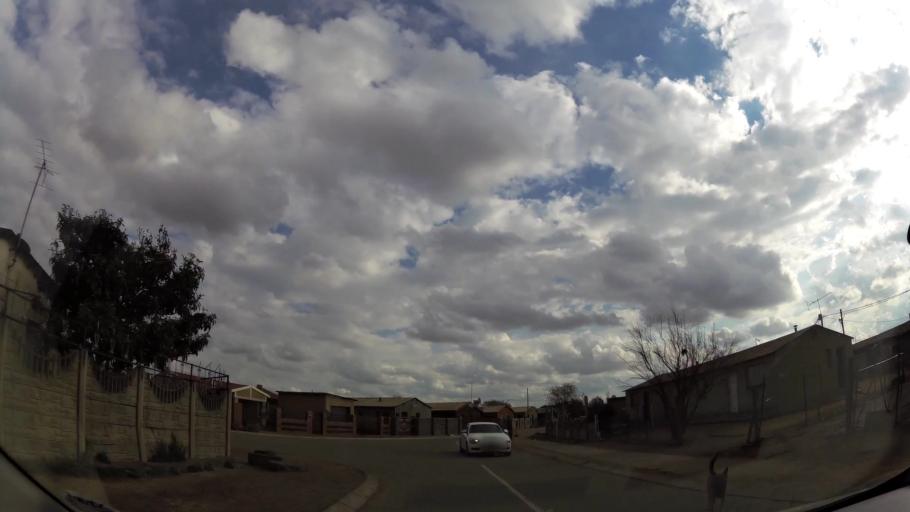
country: ZA
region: Orange Free State
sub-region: Fezile Dabi District Municipality
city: Sasolburg
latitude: -26.8405
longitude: 27.8449
